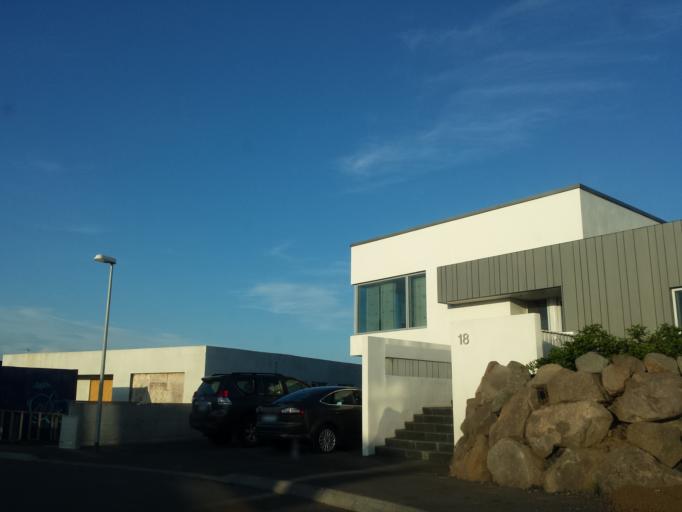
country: IS
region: Capital Region
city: Kopavogur
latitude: 64.0878
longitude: -21.8591
